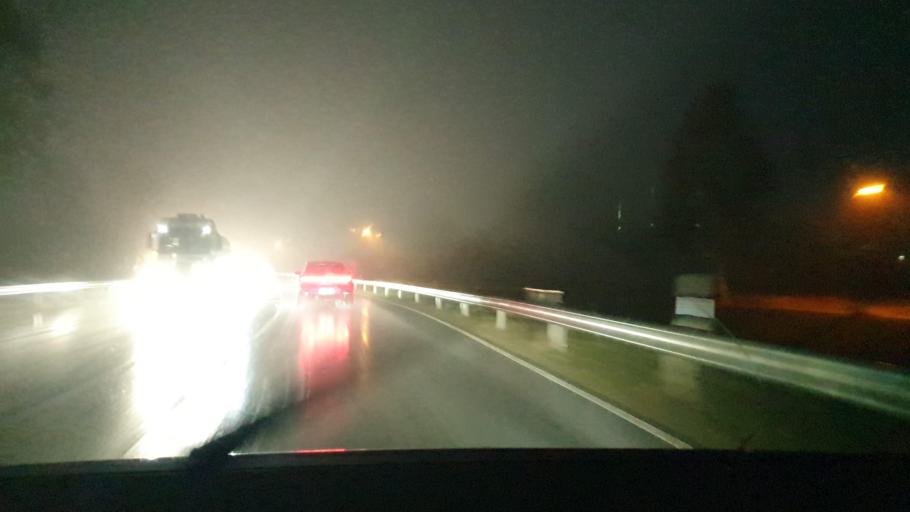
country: DE
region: Rheinland-Pfalz
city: Rennerod
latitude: 50.6190
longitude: 8.0773
